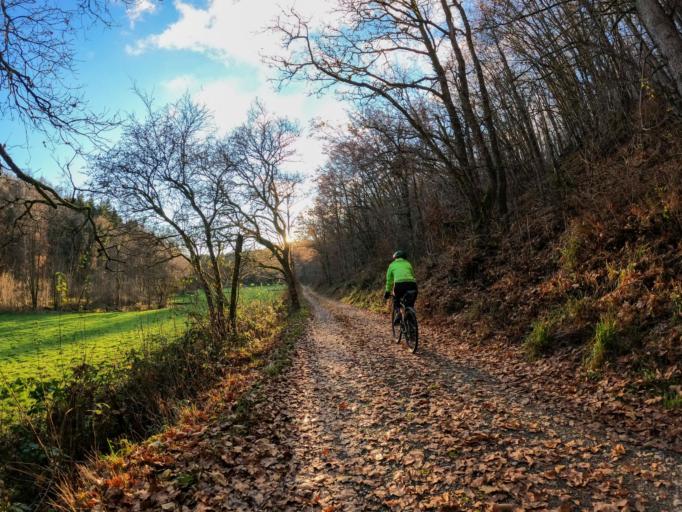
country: LU
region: Diekirch
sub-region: Canton de Wiltz
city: Bavigne
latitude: 49.9529
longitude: 5.8409
